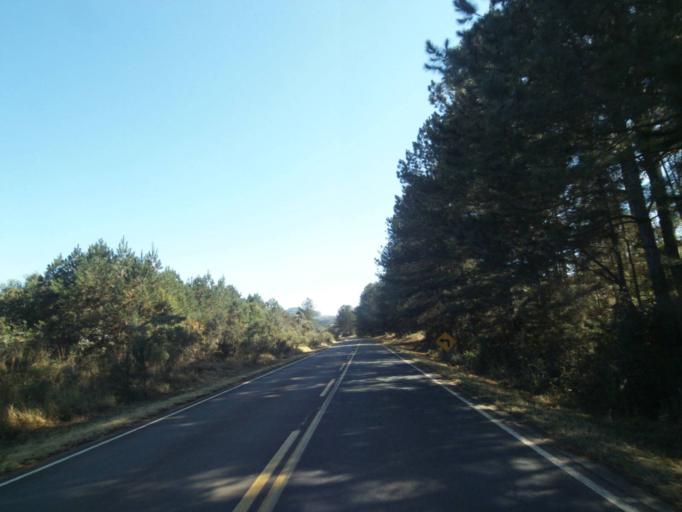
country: BR
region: Parana
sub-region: Tibagi
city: Tibagi
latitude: -24.4762
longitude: -50.4854
